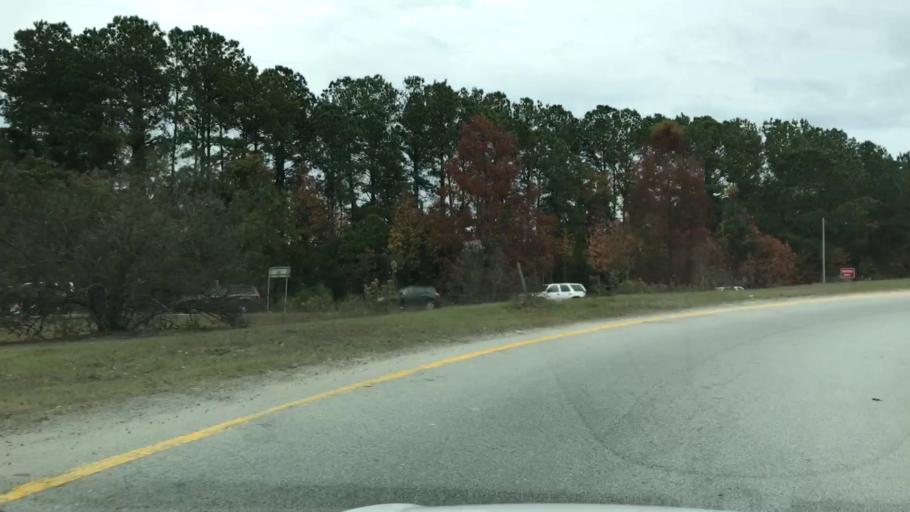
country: US
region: South Carolina
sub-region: Charleston County
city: Mount Pleasant
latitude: 32.8400
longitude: -79.8606
